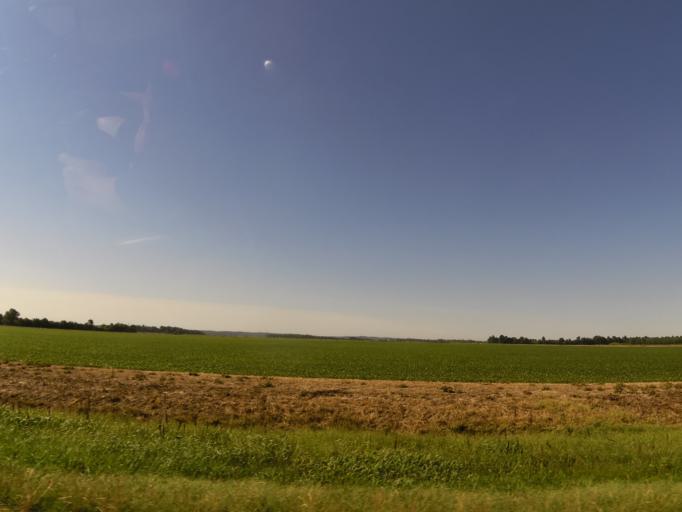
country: US
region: Arkansas
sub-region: Clay County
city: Corning
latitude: 36.4346
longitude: -90.4047
